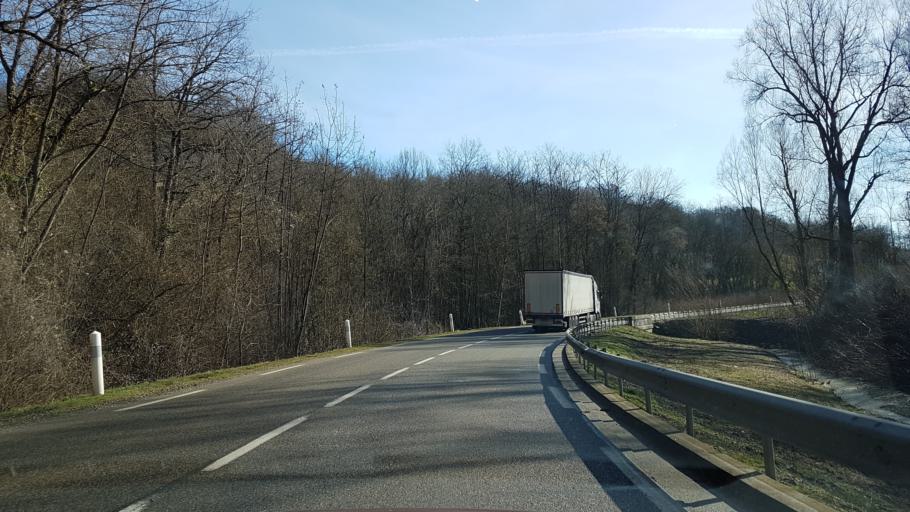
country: FR
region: Rhone-Alpes
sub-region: Departement de la Haute-Savoie
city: Frangy
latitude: 46.0262
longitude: 5.8996
